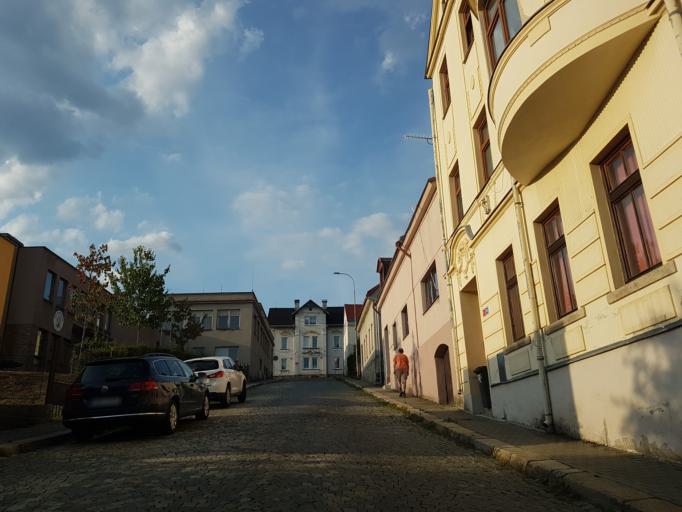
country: CZ
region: Liberecky
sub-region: Okres Jablonec nad Nisou
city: Jablonec nad Nisou
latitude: 50.7249
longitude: 15.1809
